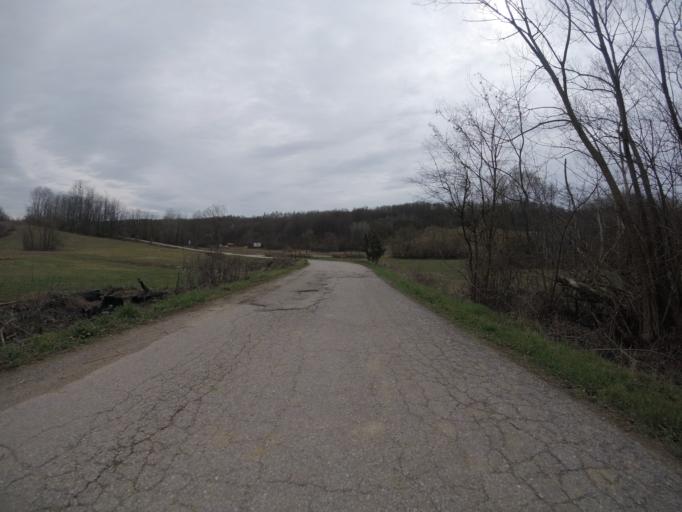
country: HR
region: Grad Zagreb
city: Strmec
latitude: 45.5871
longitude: 15.9497
